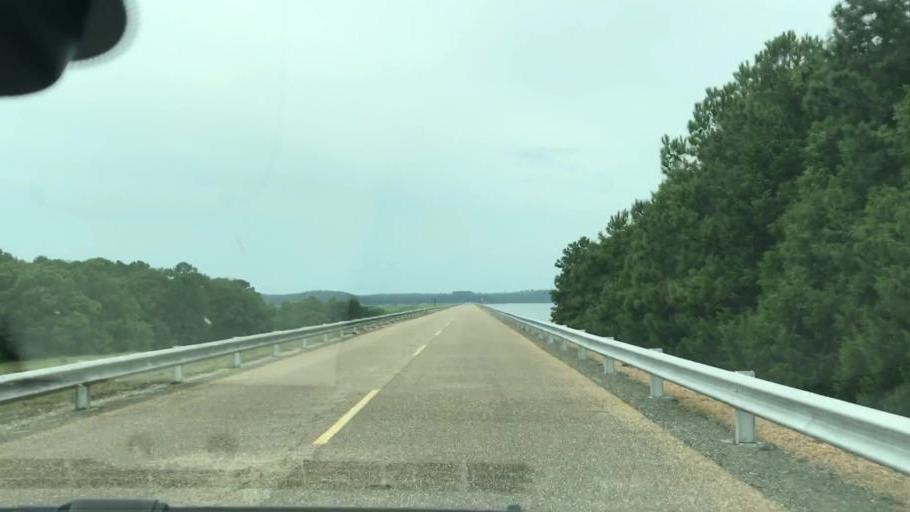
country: US
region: Georgia
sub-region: Clay County
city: Fort Gaines
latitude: 31.6303
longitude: -85.0515
